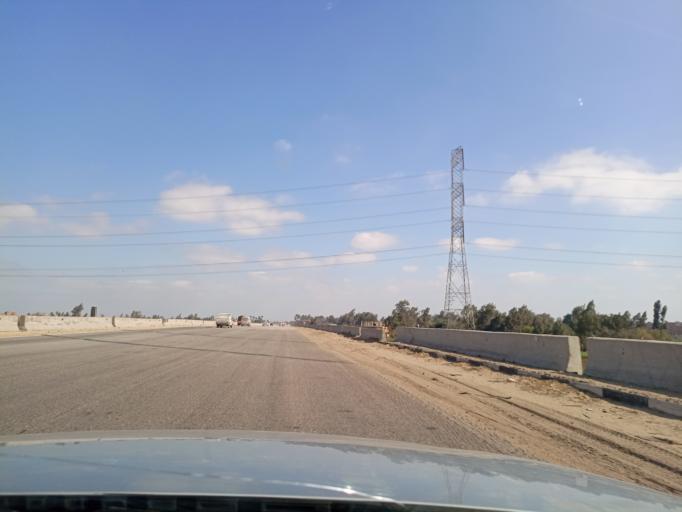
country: EG
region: Muhafazat al Qalyubiyah
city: Banha
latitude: 30.4404
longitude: 31.1125
